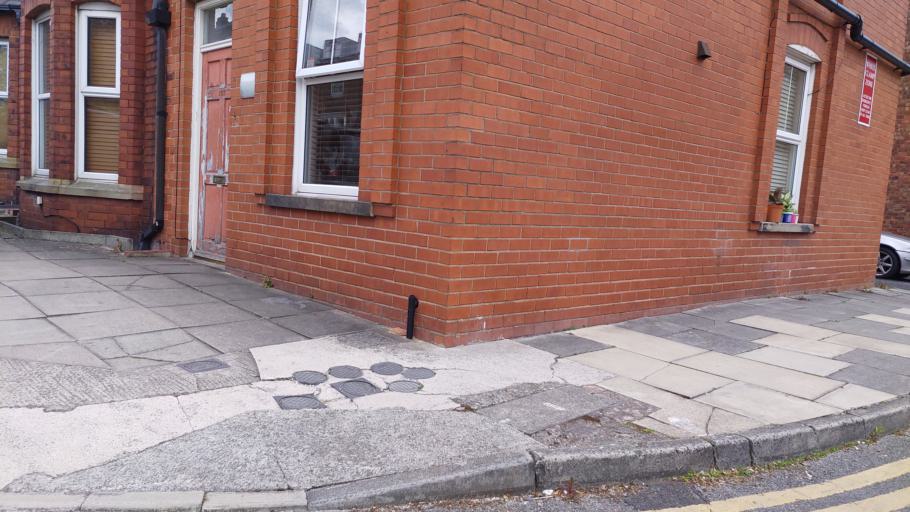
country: GB
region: England
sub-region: Borough of Wigan
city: Ince-in-Makerfield
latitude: 53.5501
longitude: -2.6292
